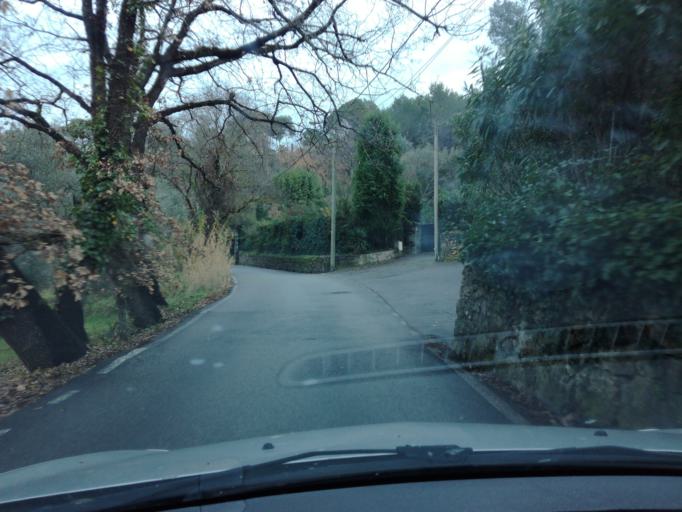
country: FR
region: Provence-Alpes-Cote d'Azur
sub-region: Departement des Alpes-Maritimes
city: Mouans-Sartoux
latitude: 43.6055
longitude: 6.9792
